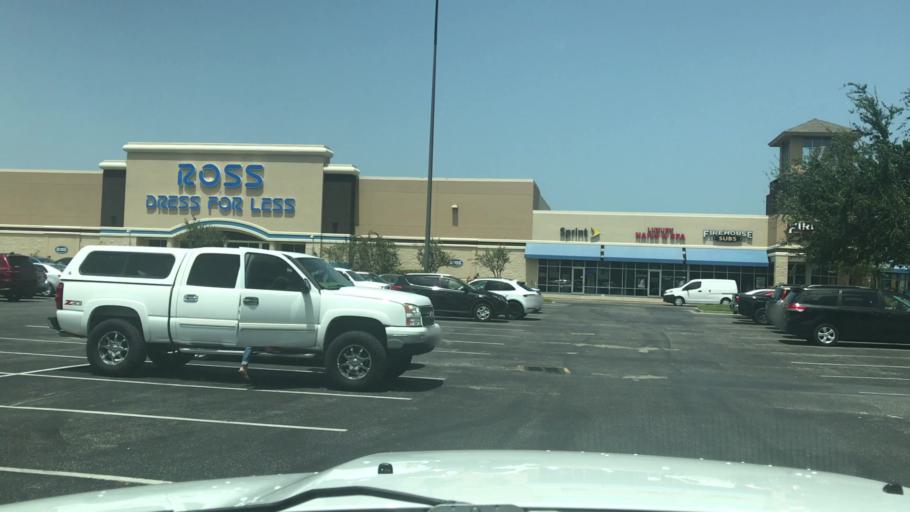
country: US
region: Florida
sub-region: Indian River County
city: West Vero Corridor
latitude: 27.6406
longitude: -80.4547
